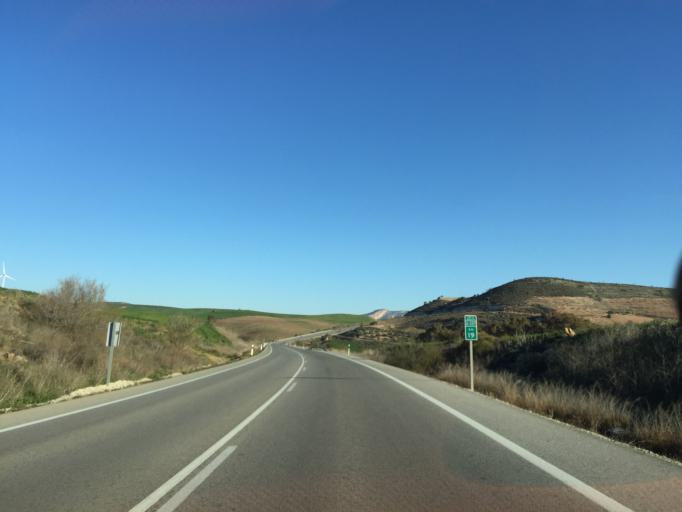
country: ES
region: Andalusia
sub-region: Provincia de Malaga
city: Ardales
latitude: 36.9040
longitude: -4.8404
